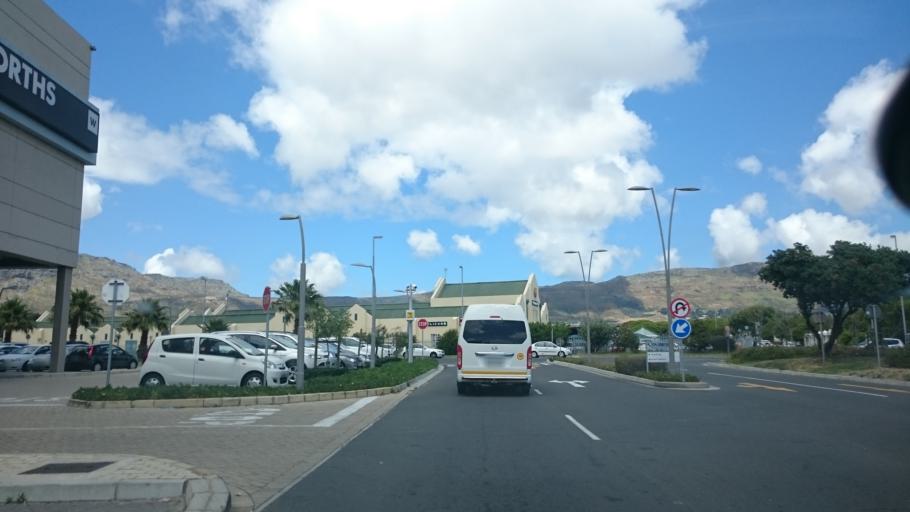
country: ZA
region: Western Cape
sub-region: City of Cape Town
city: Bergvliet
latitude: -34.0636
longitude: 18.4517
